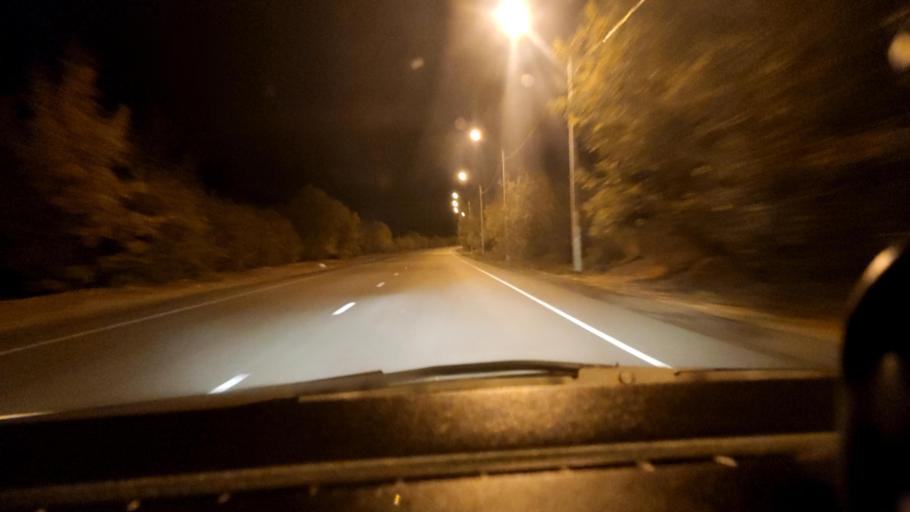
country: RU
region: Voronezj
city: Voronezh
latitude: 51.6108
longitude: 39.1794
